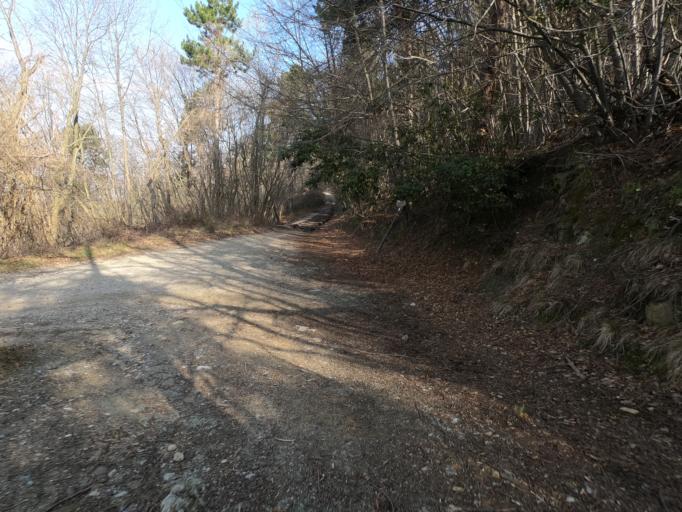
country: IT
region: Liguria
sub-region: Provincia di Savona
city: Castelvecchio di Rocca Barbena
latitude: 44.1272
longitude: 8.1393
